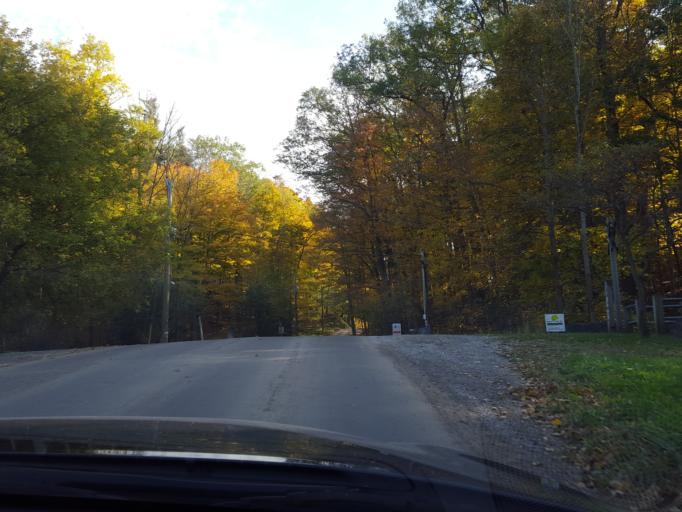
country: CA
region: Ontario
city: Ancaster
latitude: 43.2455
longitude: -80.0026
